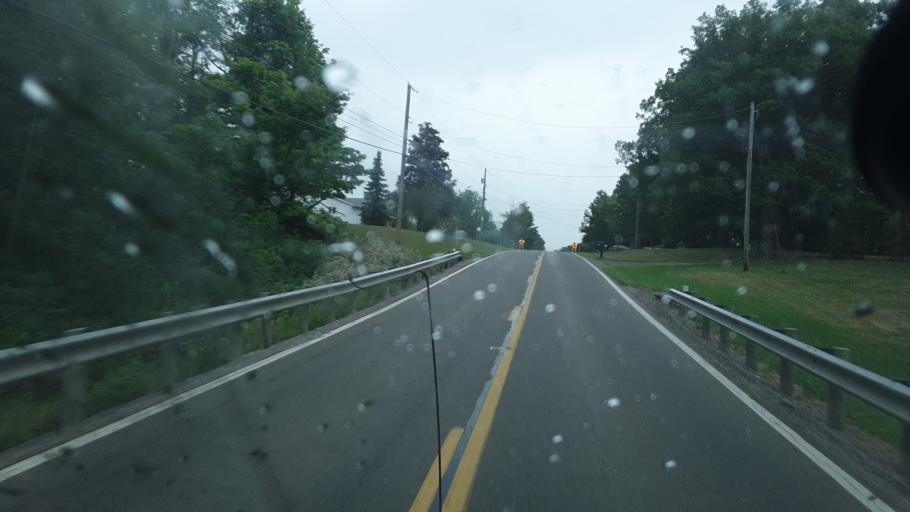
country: US
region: Ohio
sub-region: Williams County
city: Bryan
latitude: 41.4861
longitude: -84.6131
